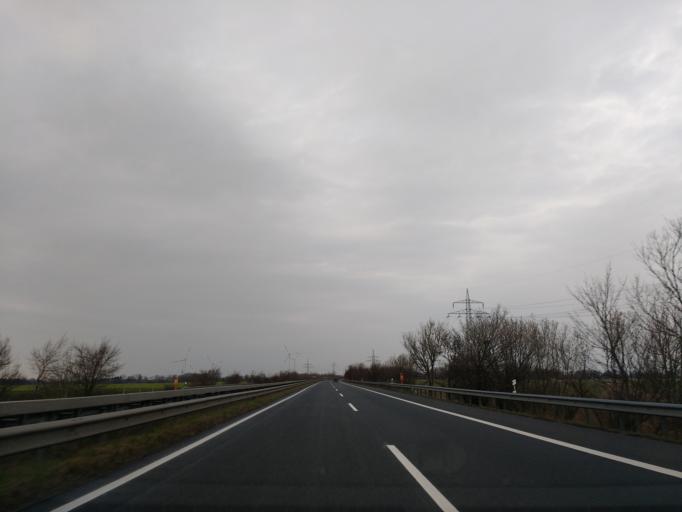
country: DE
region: Lower Saxony
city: Cuxhaven
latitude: 53.8022
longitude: 8.7073
